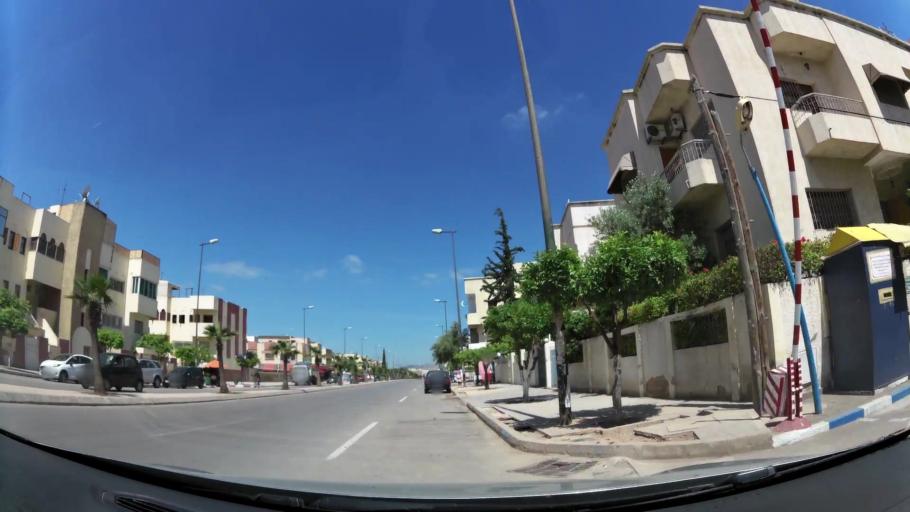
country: MA
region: Fes-Boulemane
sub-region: Fes
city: Fes
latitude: 34.0245
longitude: -5.0175
